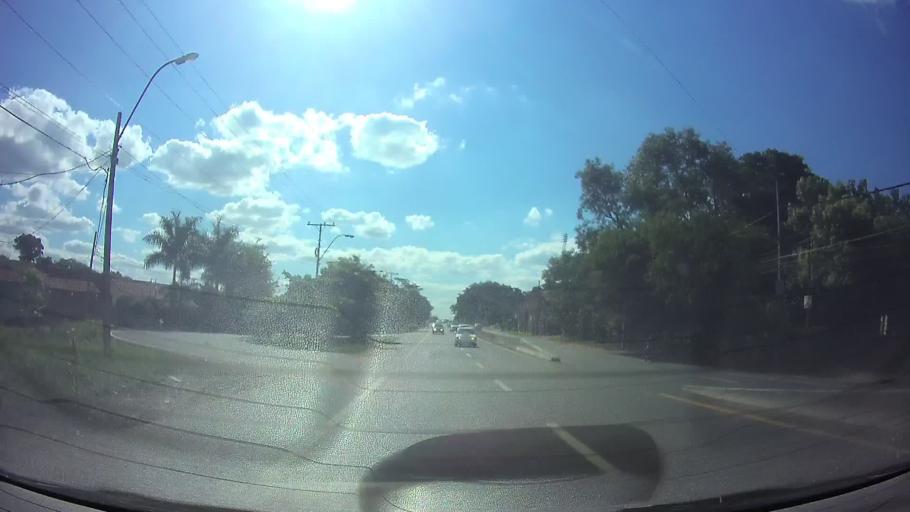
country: PY
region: Central
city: Itaugua
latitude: -25.3975
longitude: -57.3385
